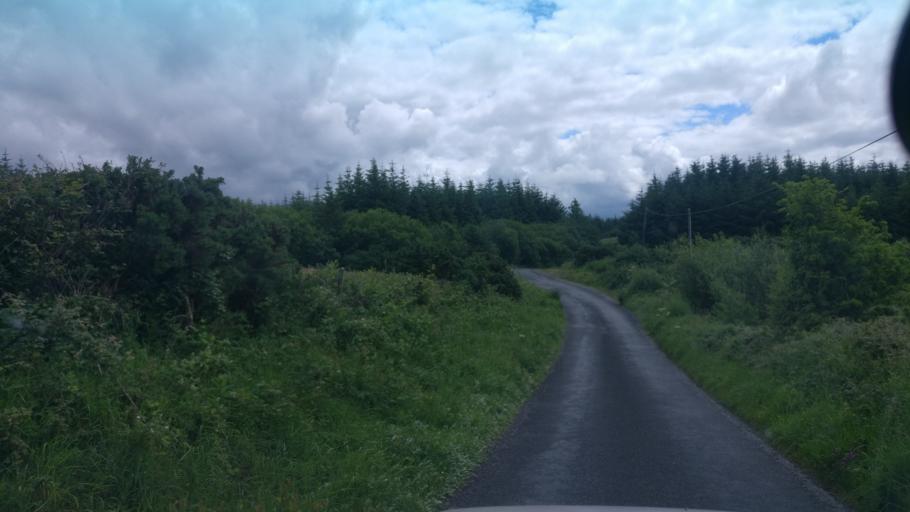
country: IE
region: Connaught
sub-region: County Galway
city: Loughrea
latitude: 53.1487
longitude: -8.5663
